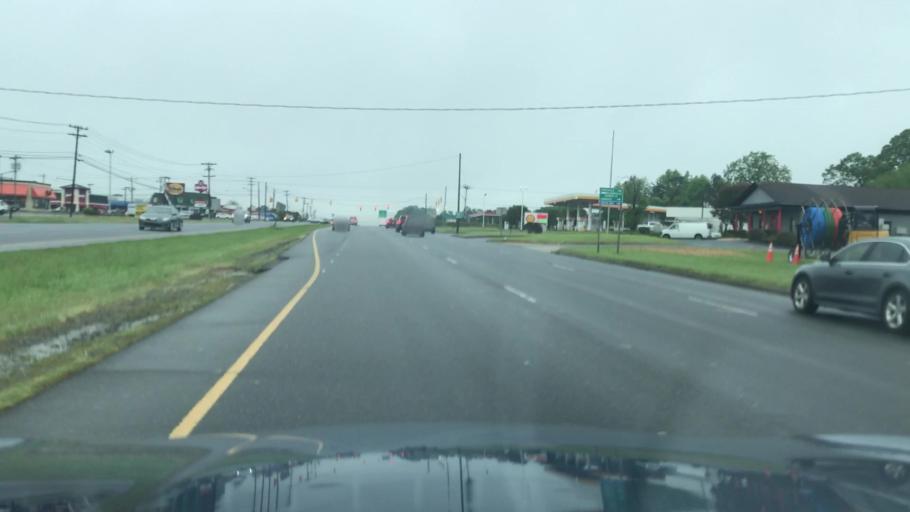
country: US
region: North Carolina
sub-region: Mecklenburg County
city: Matthews
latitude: 35.1205
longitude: -80.6998
